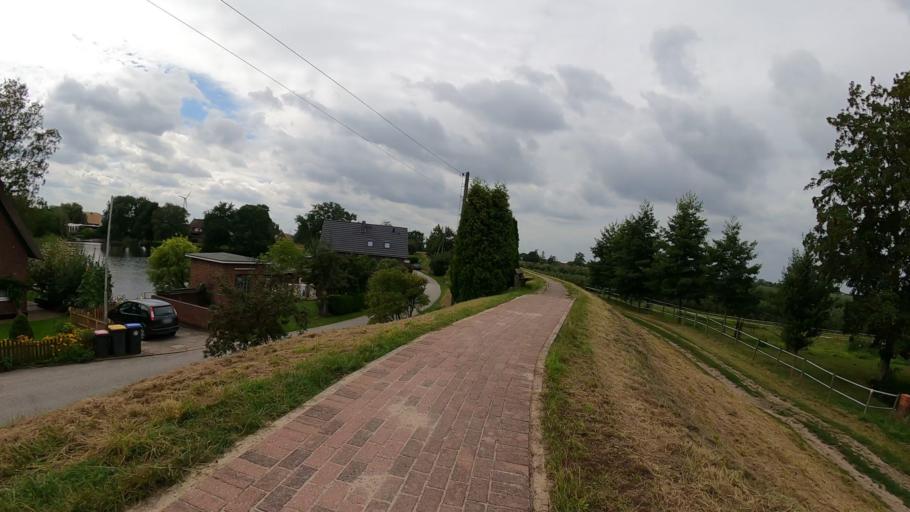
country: DE
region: Lower Saxony
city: Neu Wulmstorf
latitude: 53.5090
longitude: 9.8454
